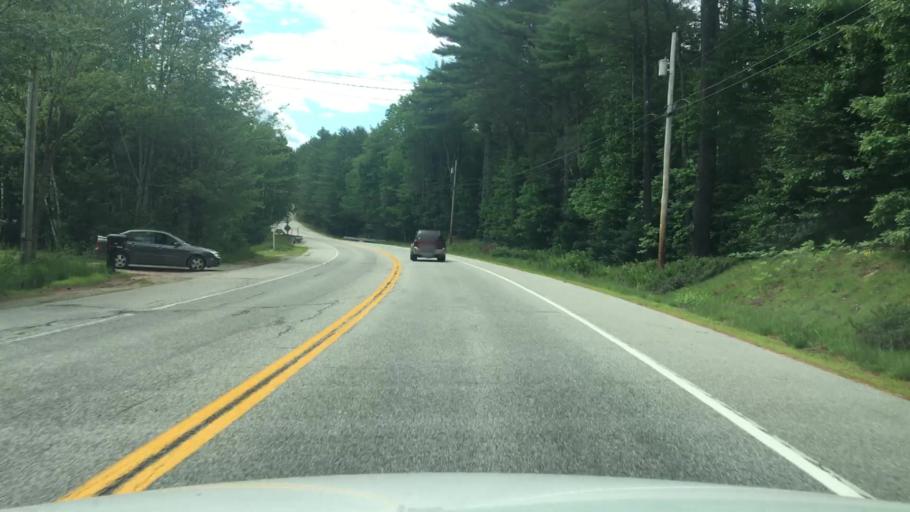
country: US
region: Maine
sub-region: Oxford County
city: West Paris
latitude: 44.3611
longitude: -70.5748
